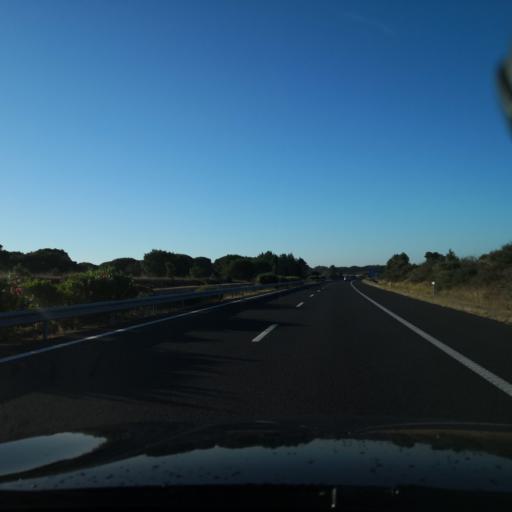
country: PT
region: Santarem
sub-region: Benavente
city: Poceirao
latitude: 38.7108
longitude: -8.6479
